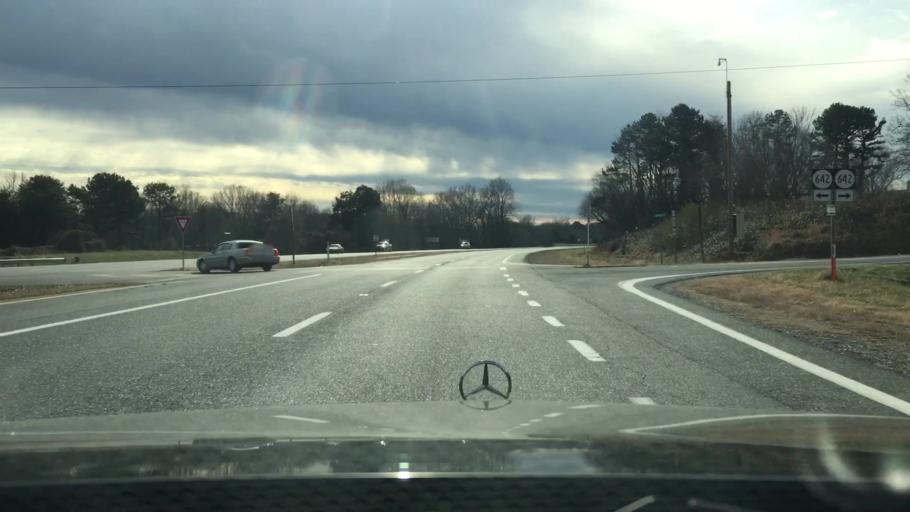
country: US
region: Virginia
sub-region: Pittsylvania County
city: Motley
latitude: 37.0650
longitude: -79.3422
